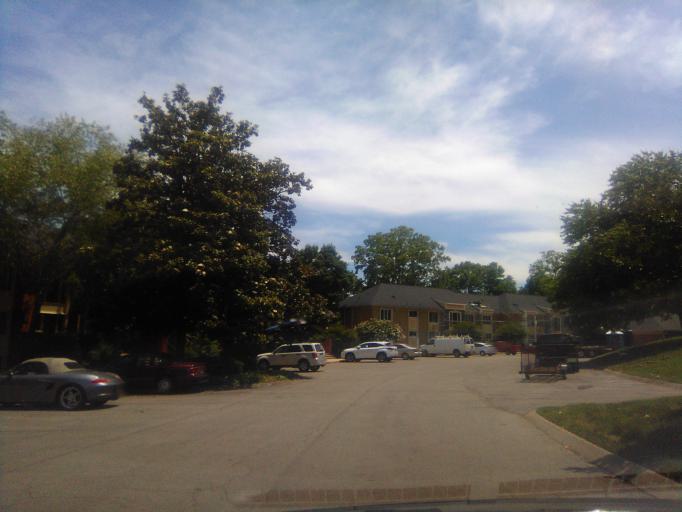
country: US
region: Tennessee
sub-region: Davidson County
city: Belle Meade
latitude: 36.1308
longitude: -86.8495
